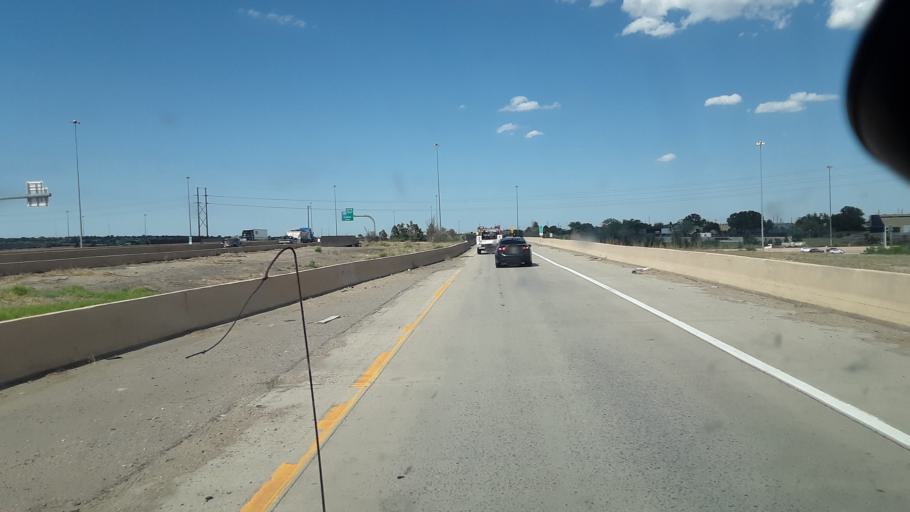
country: US
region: Colorado
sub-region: Adams County
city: Twin Lakes
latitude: 39.8150
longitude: -104.9867
